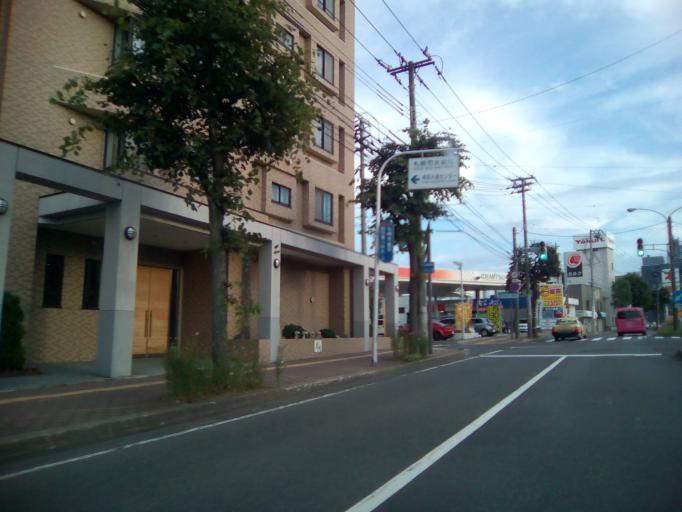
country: JP
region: Hokkaido
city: Sapporo
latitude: 43.0427
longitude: 141.3702
